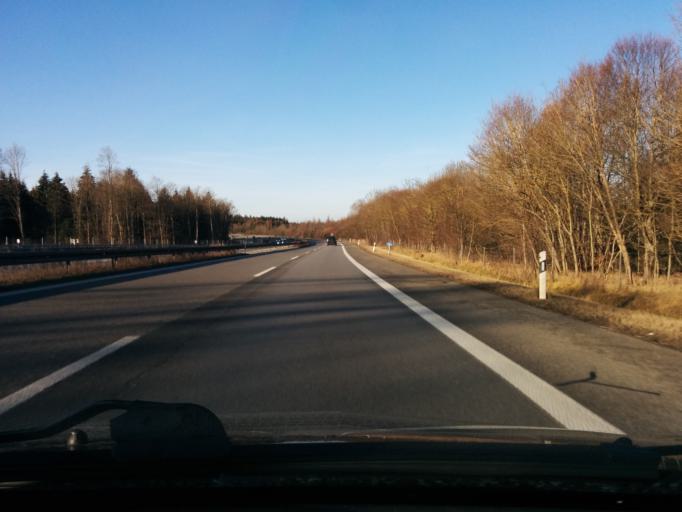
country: DE
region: Bavaria
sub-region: Upper Bavaria
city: Wessling
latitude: 48.0921
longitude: 11.2517
